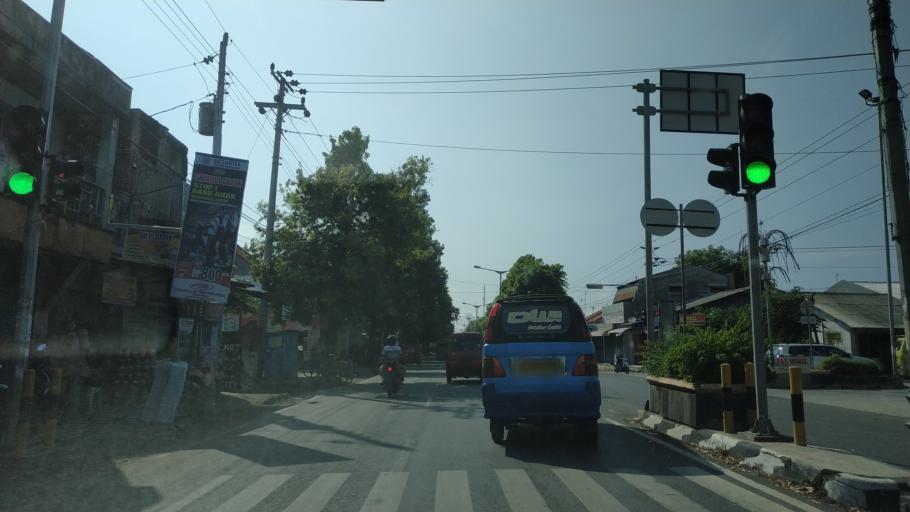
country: ID
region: Central Java
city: Petarukan
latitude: -6.8938
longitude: 109.4123
